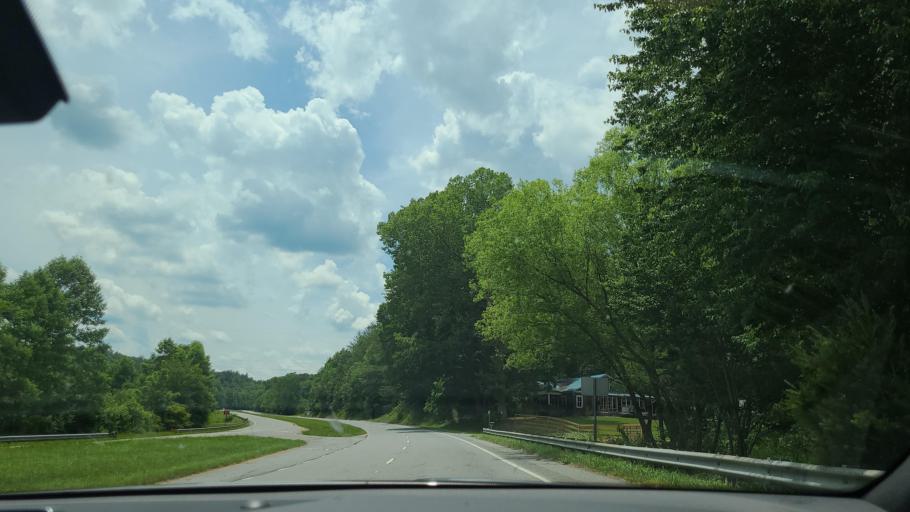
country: US
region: Georgia
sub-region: Fannin County
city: McCaysville
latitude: 35.0241
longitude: -84.2269
